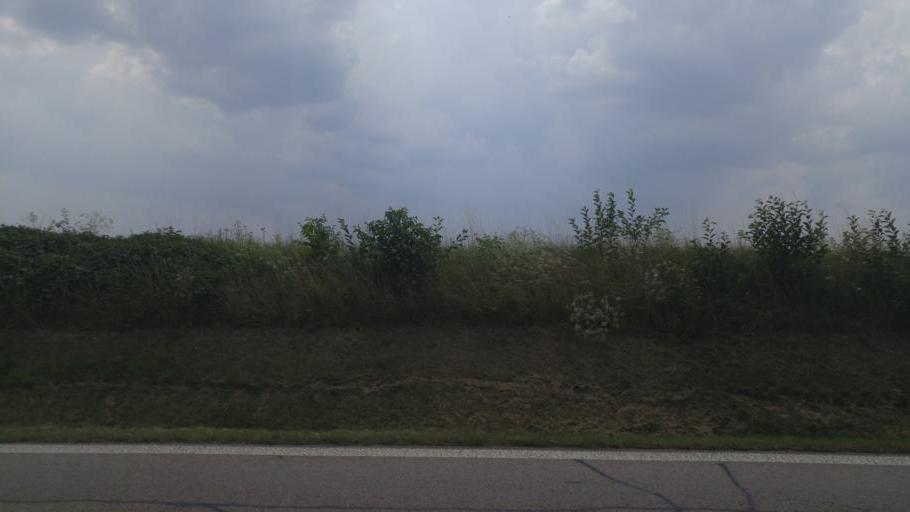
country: CZ
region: Central Bohemia
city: Hostivice
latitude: 50.0909
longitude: 14.3000
